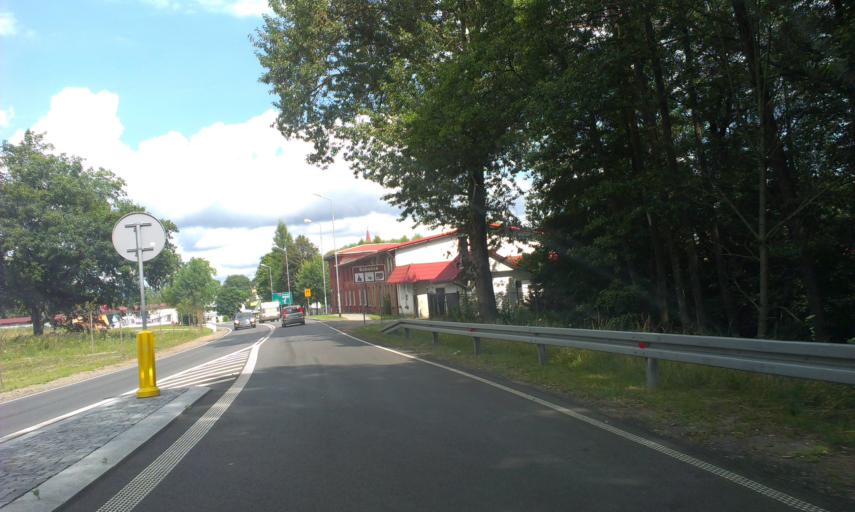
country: PL
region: West Pomeranian Voivodeship
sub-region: Powiat koszalinski
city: Bobolice
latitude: 53.9490
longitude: 16.5870
